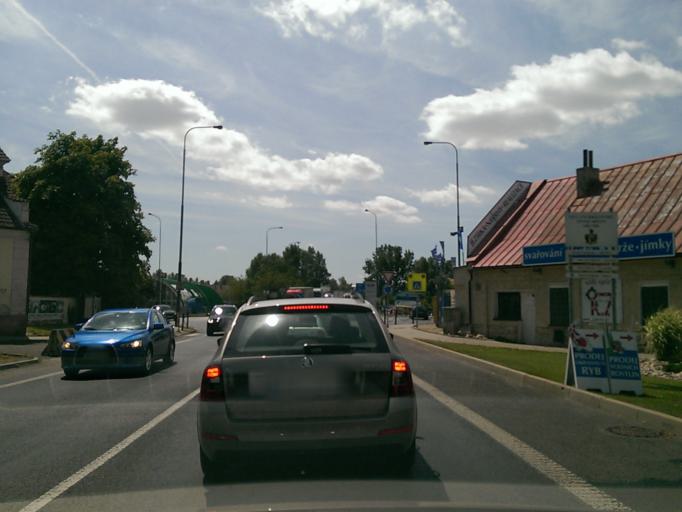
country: CZ
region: Central Bohemia
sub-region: Okres Melnik
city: Melnik
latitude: 50.3621
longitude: 14.4698
